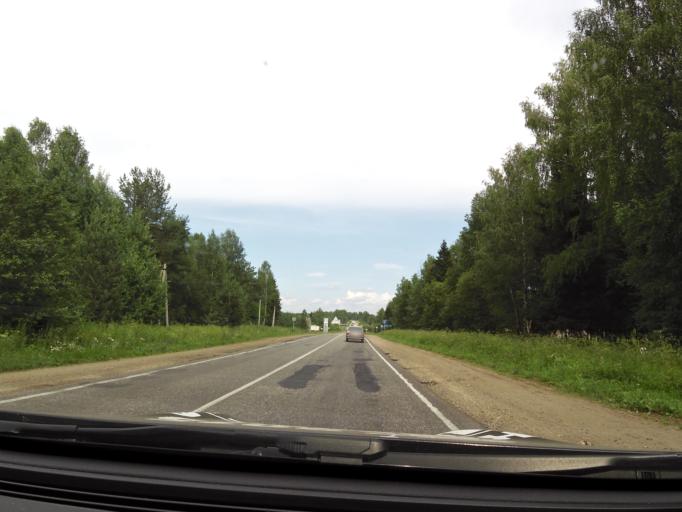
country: RU
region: Kirov
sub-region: Kirovo-Chepetskiy Rayon
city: Kirov
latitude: 58.6368
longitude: 49.8371
